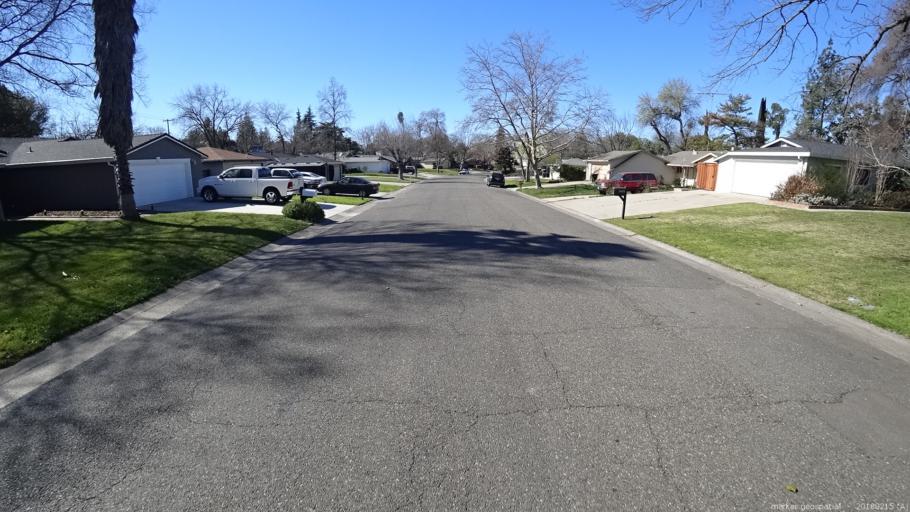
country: US
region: California
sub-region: Sacramento County
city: Fair Oaks
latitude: 38.6642
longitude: -121.3010
